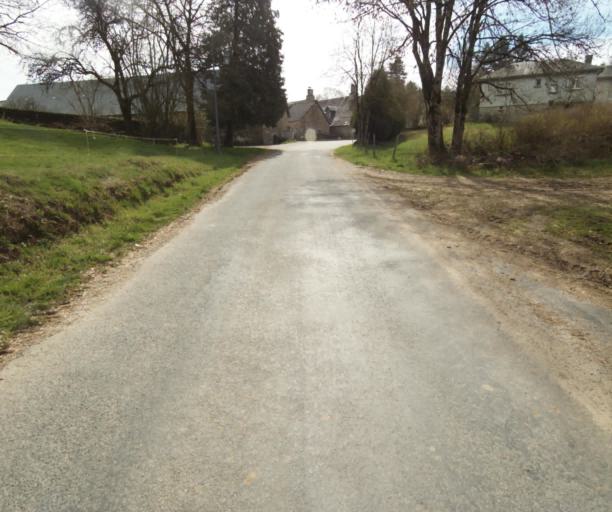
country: FR
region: Limousin
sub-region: Departement de la Correze
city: Correze
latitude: 45.3771
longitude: 1.9356
